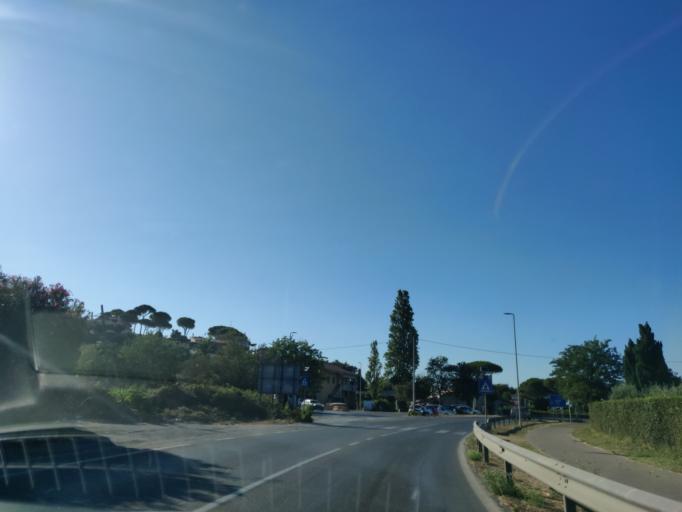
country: IT
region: Tuscany
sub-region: Provincia di Grosseto
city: Porto Ercole
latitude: 42.4259
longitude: 11.1976
